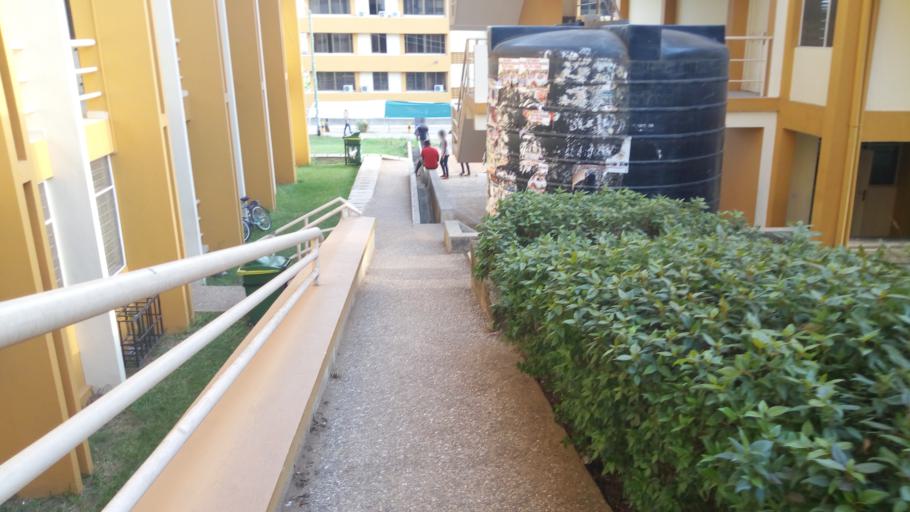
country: GH
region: Ashanti
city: Mamponteng
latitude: 6.6742
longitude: -1.5644
